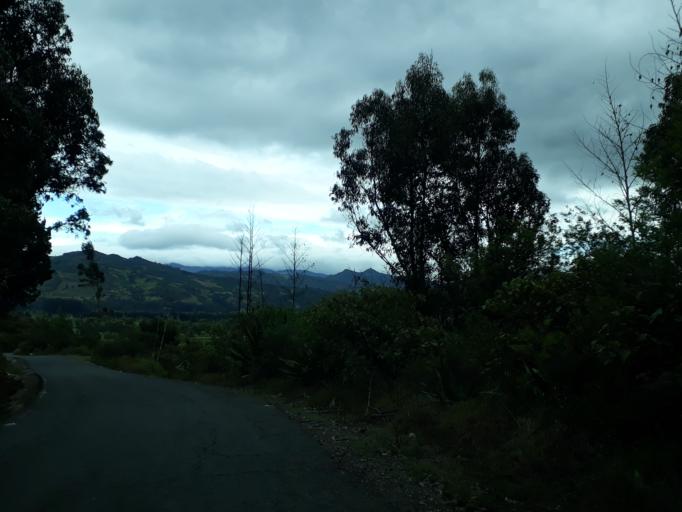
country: CO
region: Cundinamarca
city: Susa
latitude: 5.4029
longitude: -73.7684
